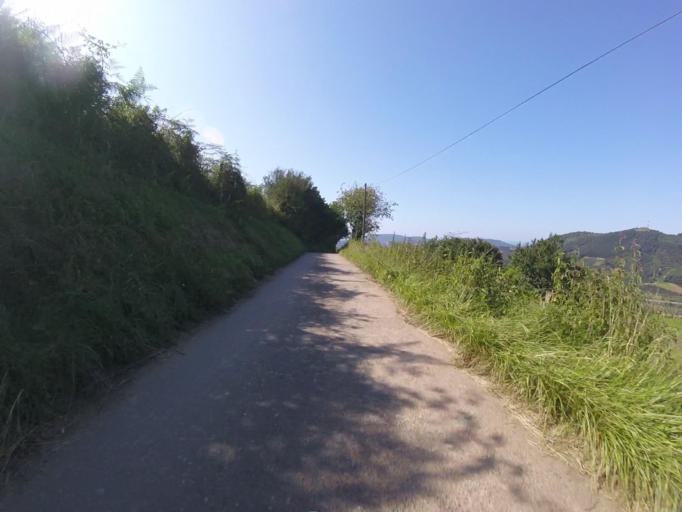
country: ES
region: Basque Country
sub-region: Provincia de Guipuzcoa
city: Astigarraga
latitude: 43.2767
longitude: -1.9305
